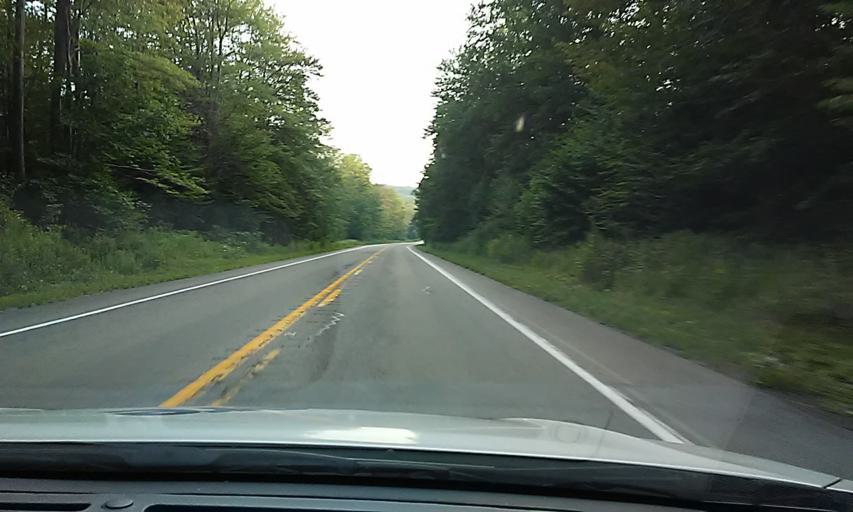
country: US
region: Pennsylvania
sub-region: Warren County
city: Sheffield
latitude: 41.5602
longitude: -78.9936
